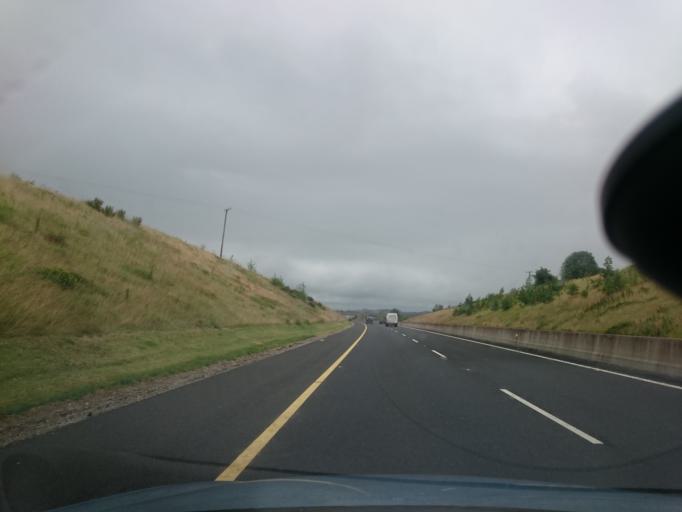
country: IE
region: Leinster
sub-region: Kildare
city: Castledermot
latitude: 52.9358
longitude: -6.8582
